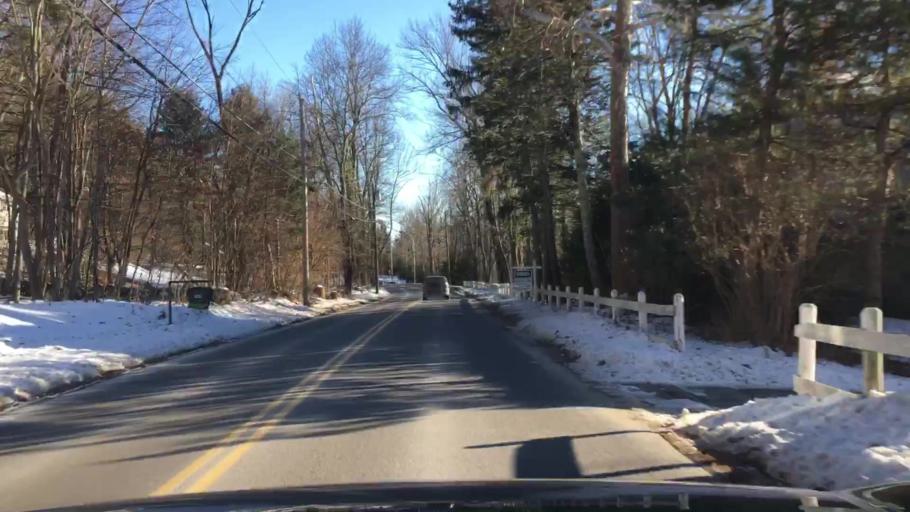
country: US
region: New Hampshire
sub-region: Hillsborough County
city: Milford
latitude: 42.8328
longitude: -71.5920
